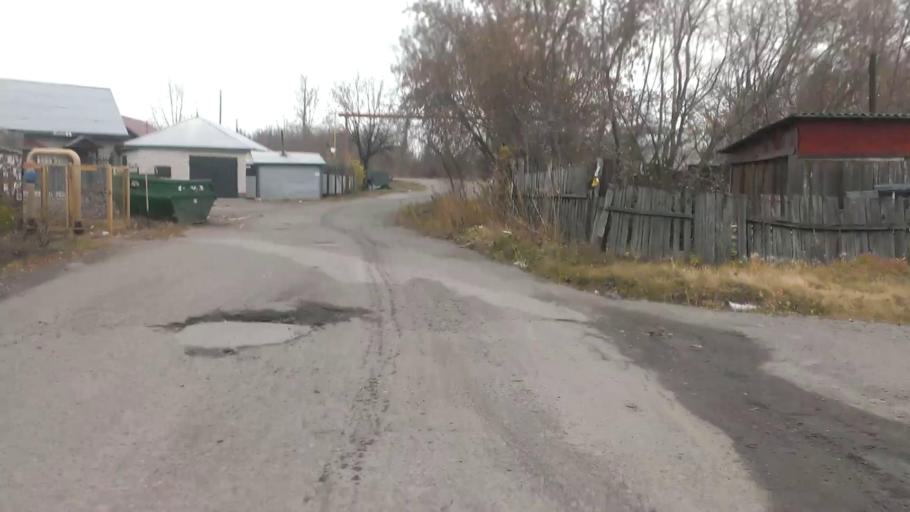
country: RU
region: Altai Krai
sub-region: Gorod Barnaulskiy
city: Barnaul
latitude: 53.3536
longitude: 83.7539
